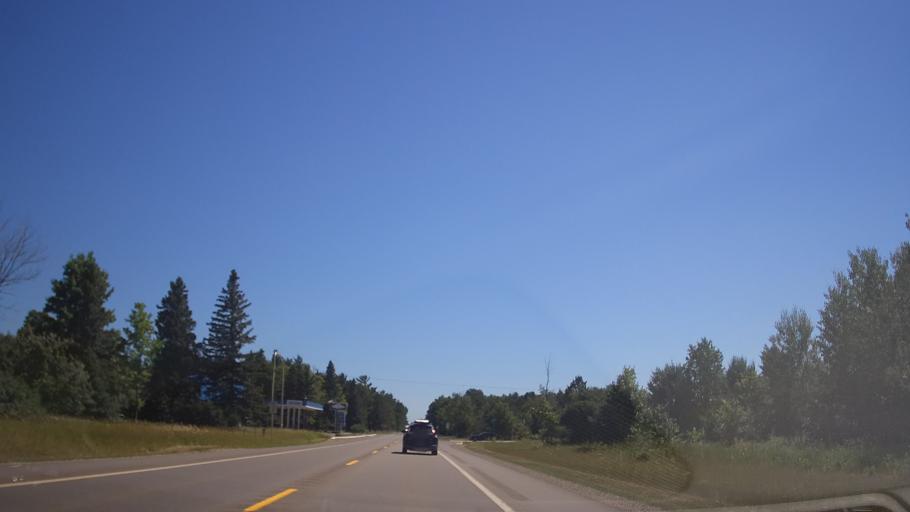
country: US
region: Michigan
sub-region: Cheboygan County
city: Indian River
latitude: 45.5953
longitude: -84.7827
